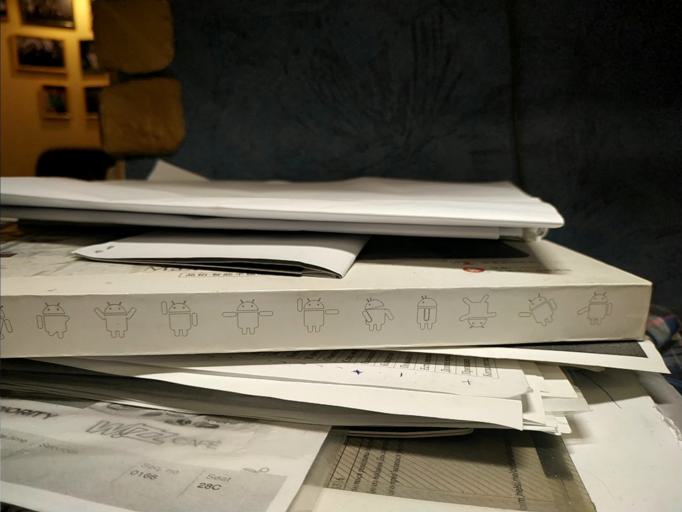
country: RU
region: Tverskaya
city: Zubtsov
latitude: 56.0829
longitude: 34.7870
